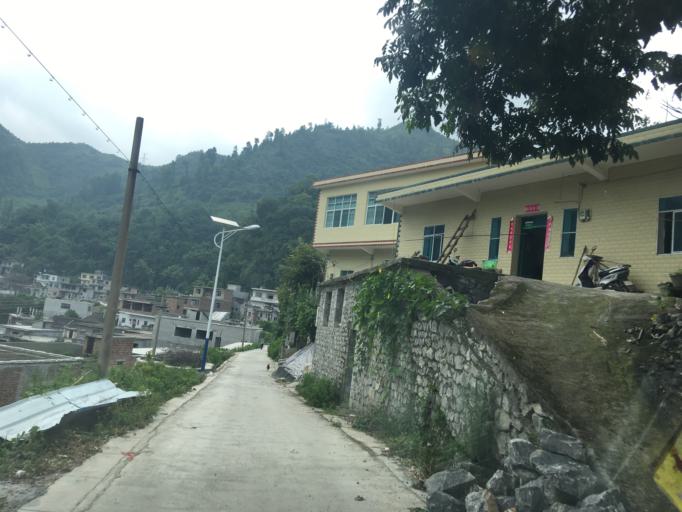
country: CN
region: Guangxi Zhuangzu Zizhiqu
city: Xinzhou
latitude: 25.0733
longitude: 105.7243
